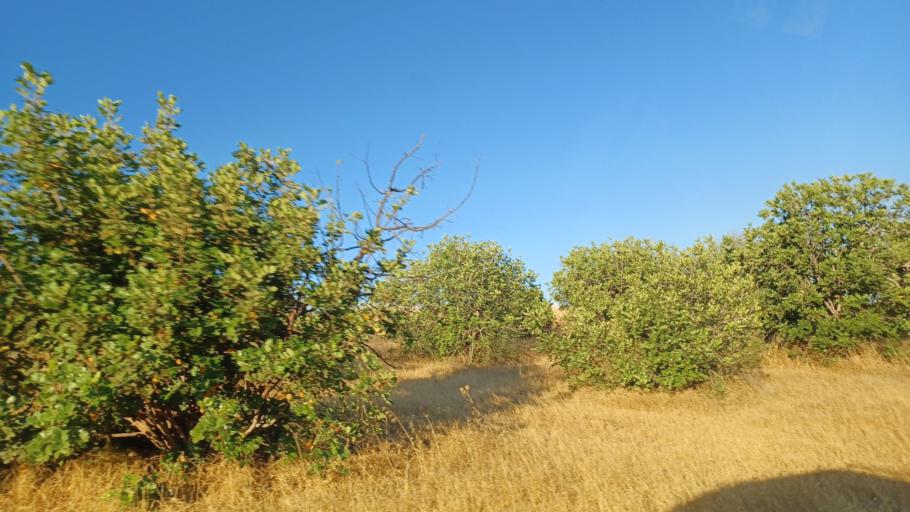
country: CY
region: Larnaka
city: Troulloi
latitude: 35.0288
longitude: 33.6494
